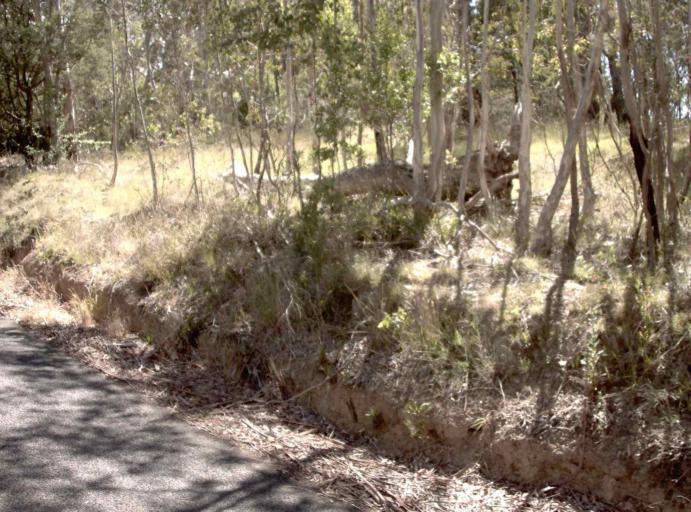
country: AU
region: New South Wales
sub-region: Bombala
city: Bombala
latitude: -37.0582
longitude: 148.8026
